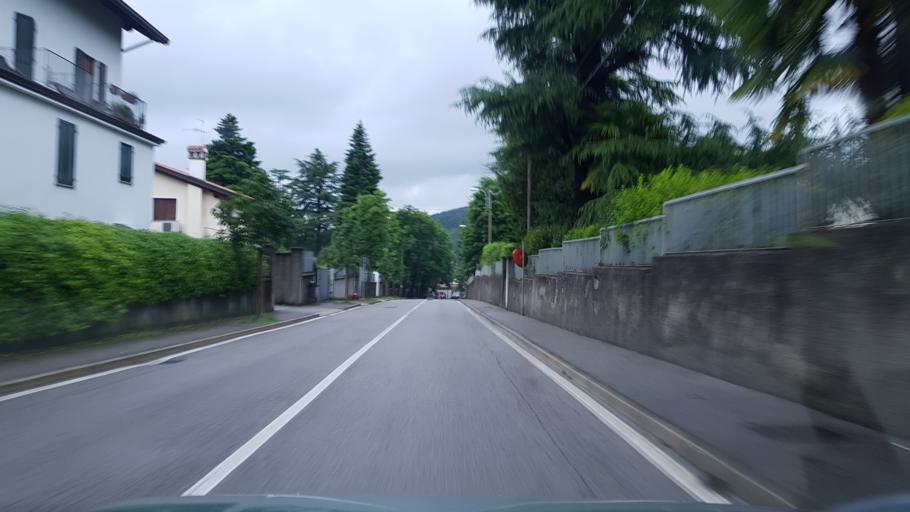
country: IT
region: Friuli Venezia Giulia
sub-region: Provincia di Gorizia
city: Gorizia
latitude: 45.9533
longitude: 13.6186
